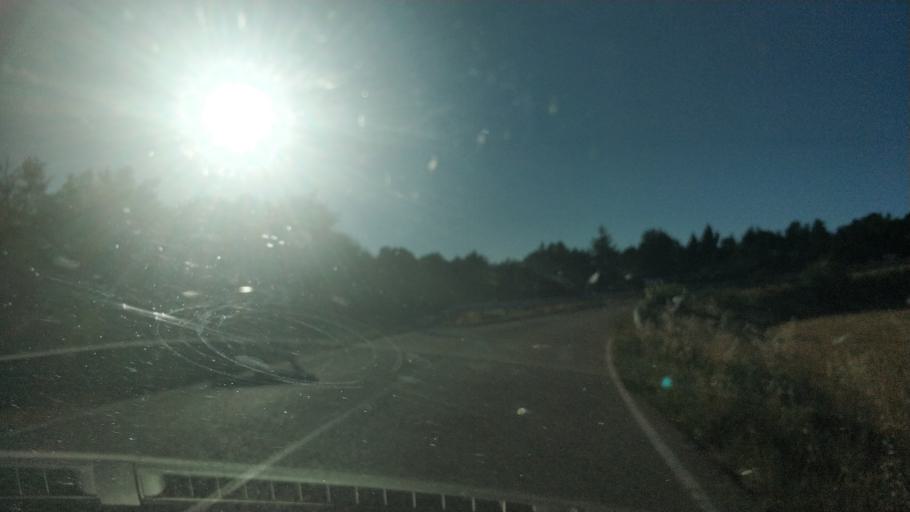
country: ES
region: Castille and Leon
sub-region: Provincia de Soria
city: Liceras
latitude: 41.4428
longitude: -3.2161
